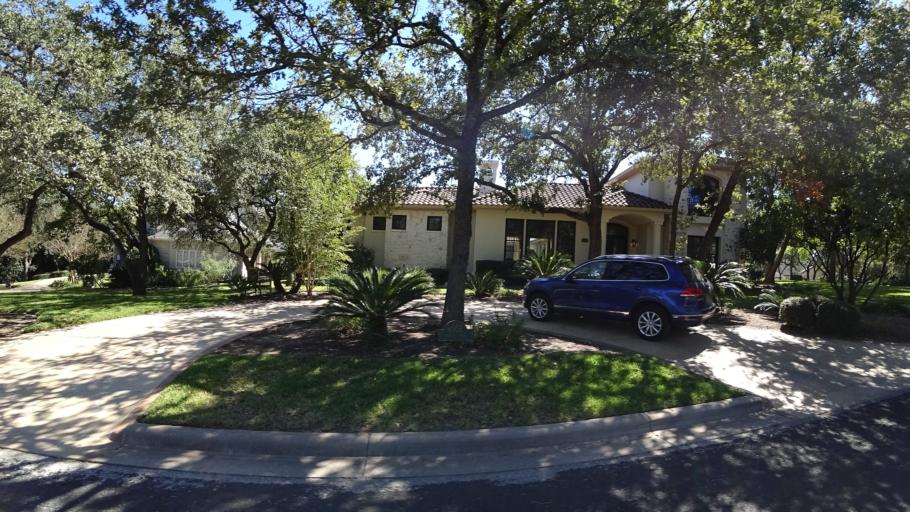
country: US
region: Texas
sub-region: Travis County
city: West Lake Hills
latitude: 30.3236
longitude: -97.7835
